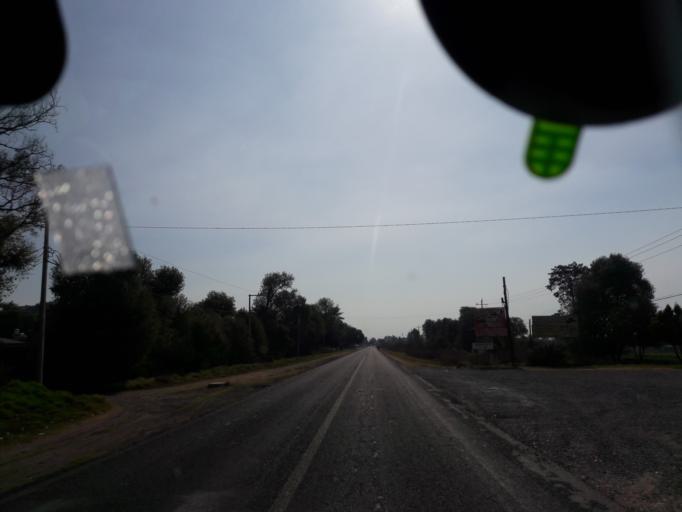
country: MX
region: Tlaxcala
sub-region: Ixtacuixtla de Mariano Matamoros
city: Santa Justina Ecatepec
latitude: 19.3084
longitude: -98.3616
